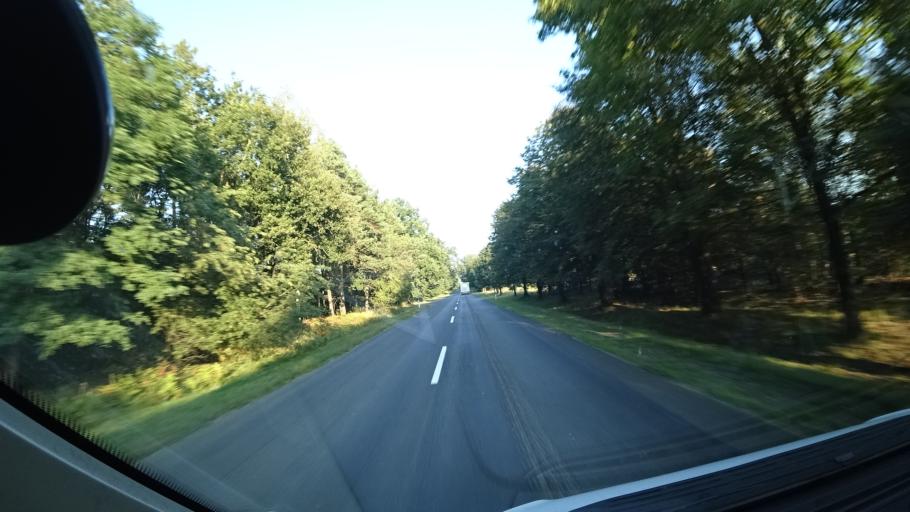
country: PL
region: Opole Voivodeship
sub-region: Powiat kedzierzynsko-kozielski
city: Dziergowice
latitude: 50.2811
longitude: 18.3328
